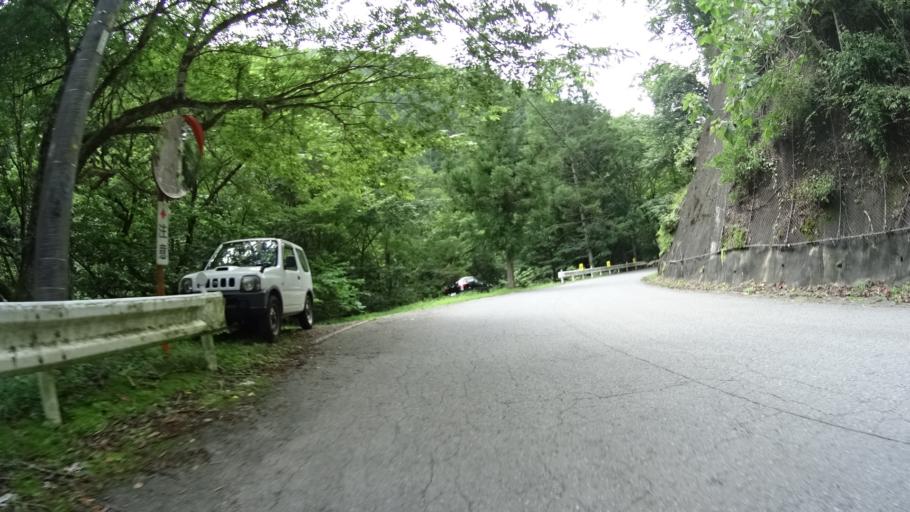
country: JP
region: Nagano
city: Saku
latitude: 36.0662
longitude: 138.6975
